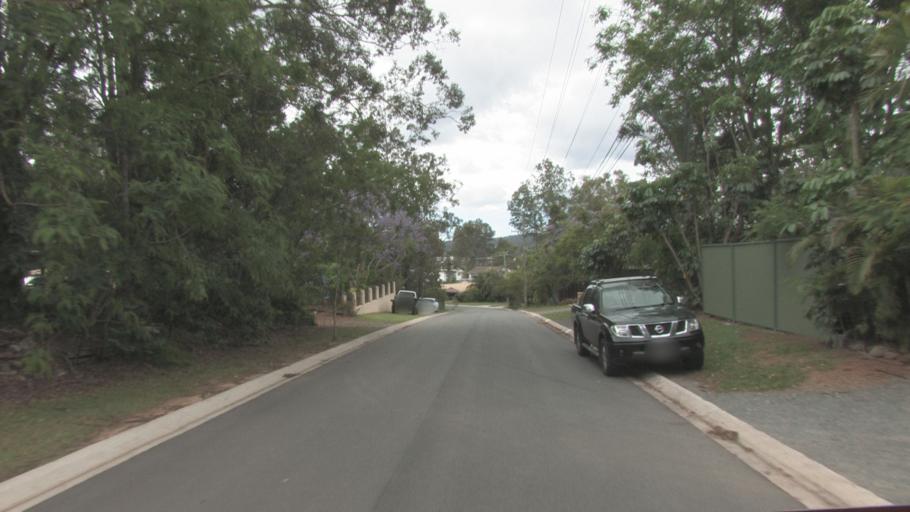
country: AU
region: Queensland
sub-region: Logan
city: Slacks Creek
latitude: -27.6678
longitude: 153.1716
